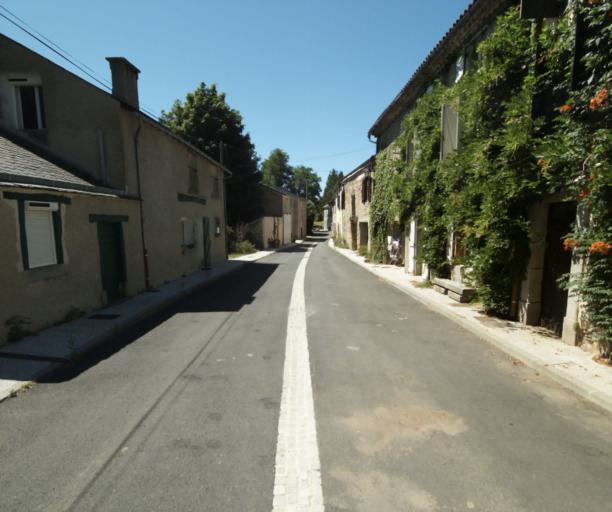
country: FR
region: Midi-Pyrenees
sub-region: Departement du Tarn
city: Dourgne
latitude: 43.4317
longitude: 2.1512
